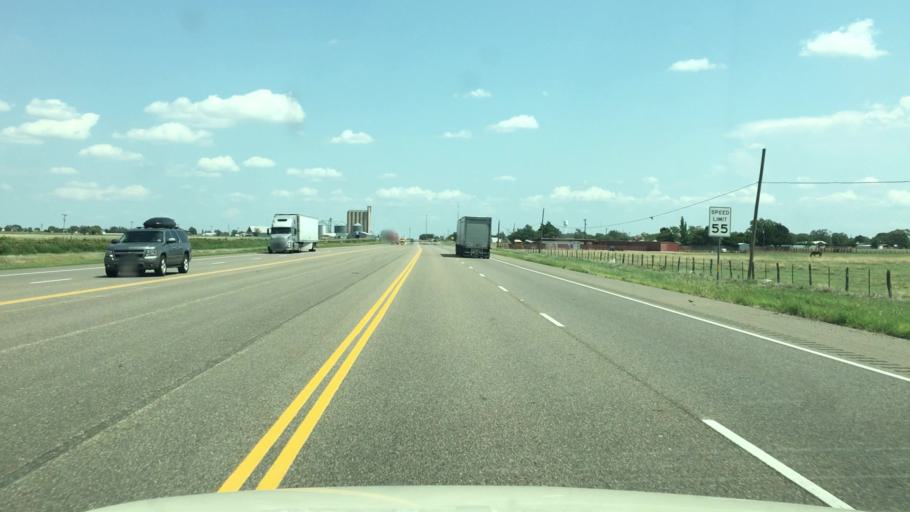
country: US
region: Texas
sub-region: Armstrong County
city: Claude
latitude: 35.1164
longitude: -101.3735
